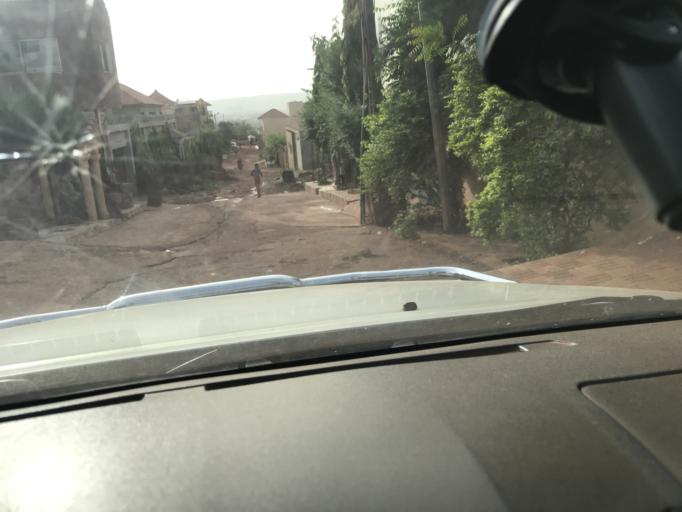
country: ML
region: Bamako
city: Bamako
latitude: 12.5884
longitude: -8.0068
